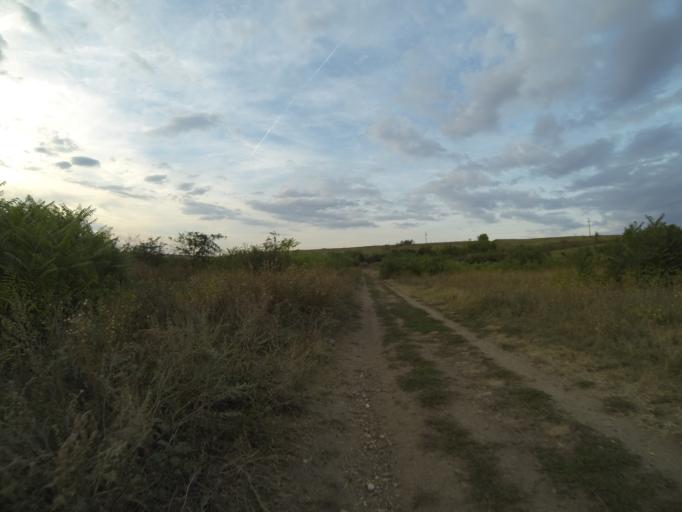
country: RO
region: Dolj
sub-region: Comuna Ceratu
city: Ceratu
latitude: 44.0909
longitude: 23.6695
